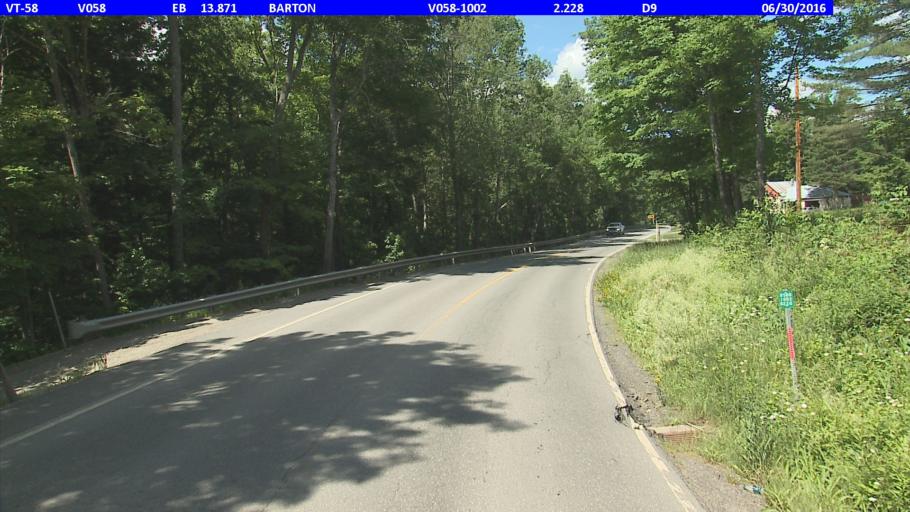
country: US
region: Vermont
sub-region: Orleans County
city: Newport
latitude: 44.8044
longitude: -72.1725
